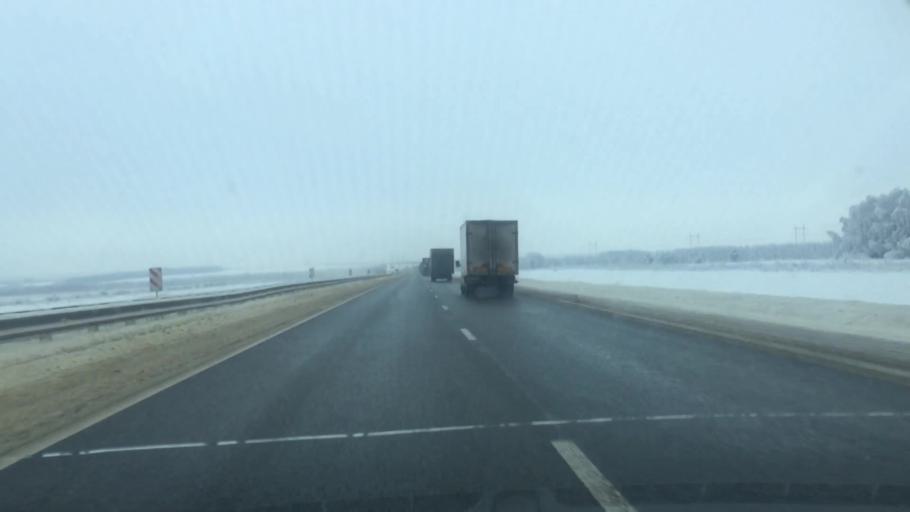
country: RU
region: Lipetsk
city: Yelets
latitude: 52.7417
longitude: 38.4771
